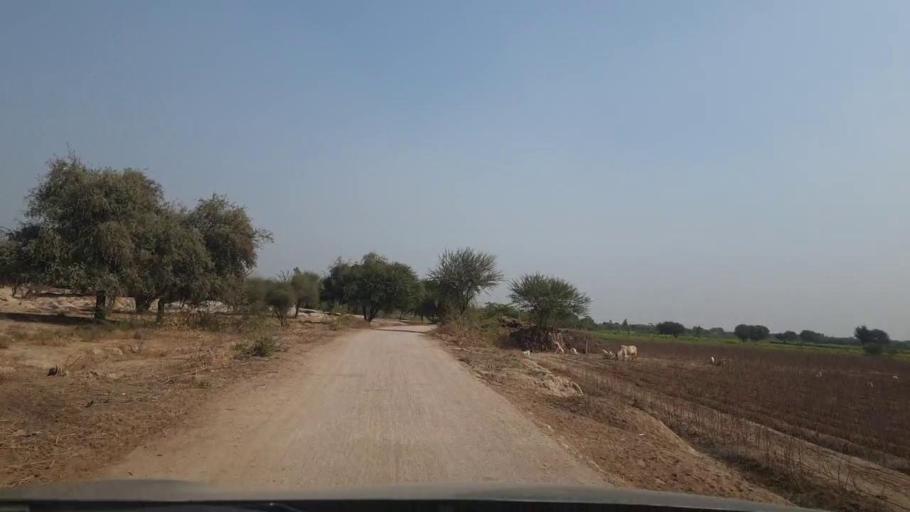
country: PK
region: Sindh
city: Tando Allahyar
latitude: 25.5591
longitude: 68.8406
